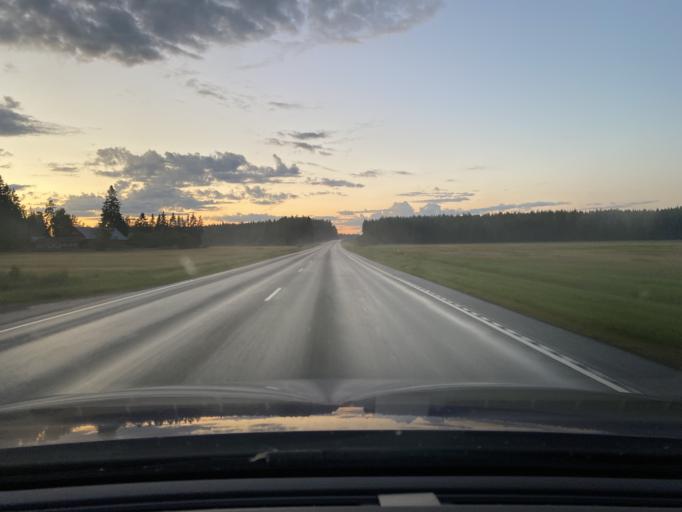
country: FI
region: Varsinais-Suomi
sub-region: Loimaa
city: Aura
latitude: 60.6941
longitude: 22.5636
